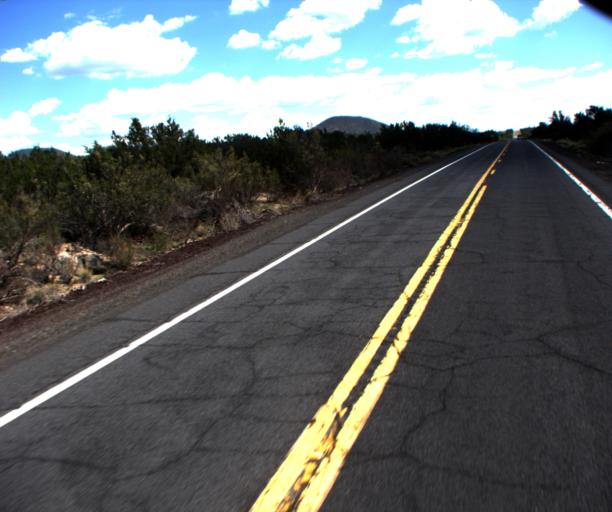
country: US
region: Arizona
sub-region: Coconino County
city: Williams
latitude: 35.4352
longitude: -112.1713
